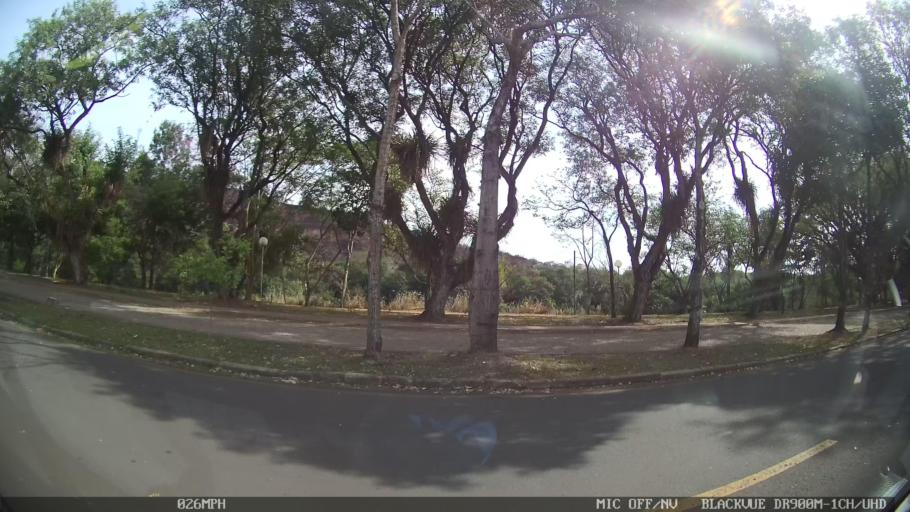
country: BR
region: Sao Paulo
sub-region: Piracicaba
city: Piracicaba
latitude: -22.7128
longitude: -47.6760
